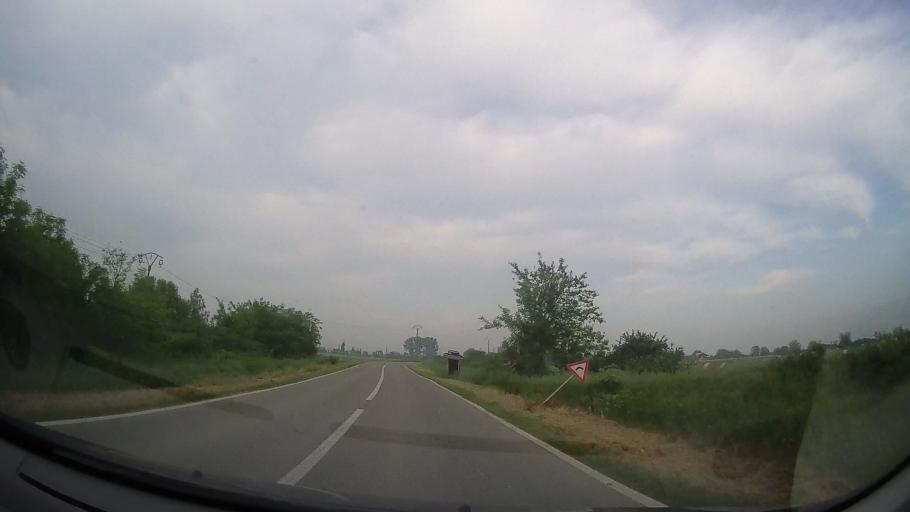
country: RO
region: Timis
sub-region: Comuna Parta
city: Parta
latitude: 45.6463
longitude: 21.1376
